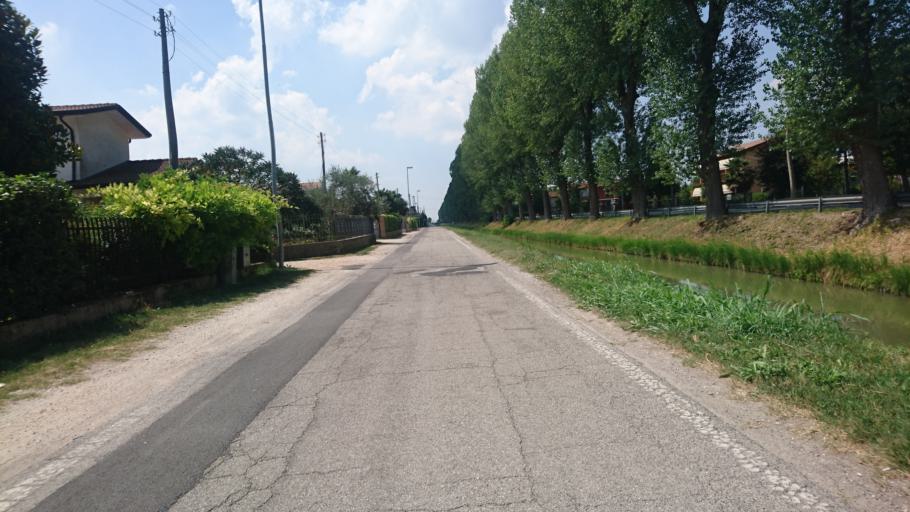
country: IT
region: Veneto
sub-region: Provincia di Padova
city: Sant'Angelo di Piove di Sacco
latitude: 45.3028
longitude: 12.0128
